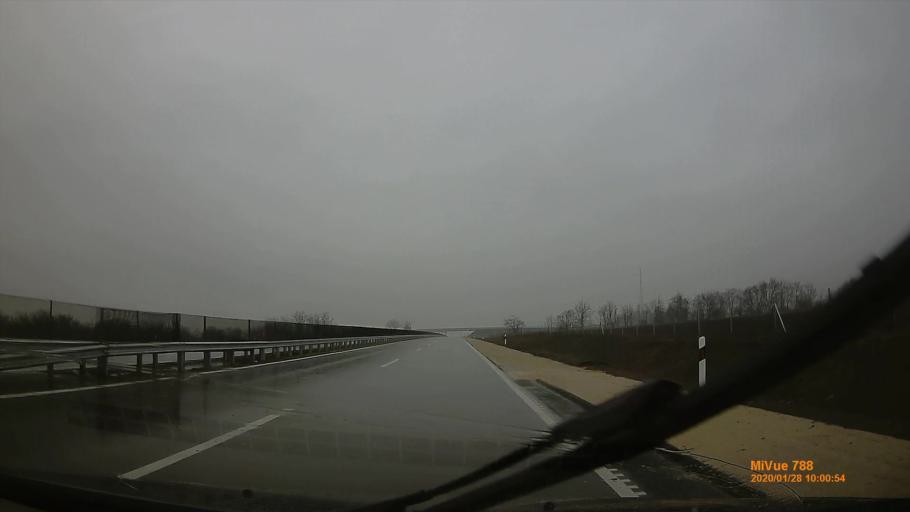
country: HU
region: Pest
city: Albertirsa
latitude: 47.2677
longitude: 19.6108
